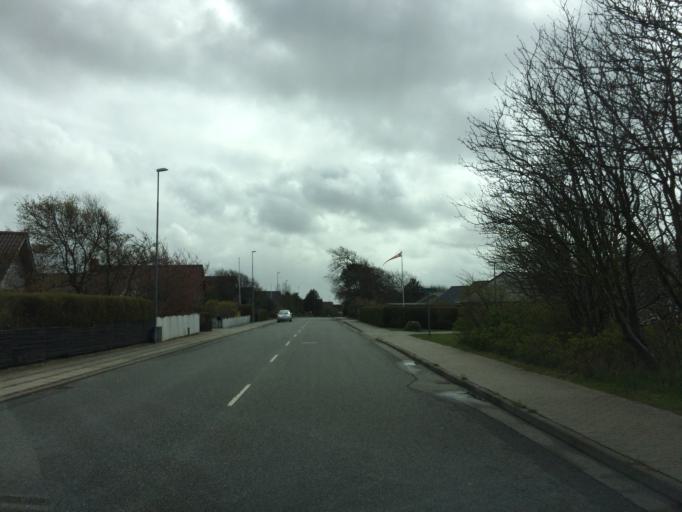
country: DK
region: South Denmark
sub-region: Fano Kommune
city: Nordby
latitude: 55.5324
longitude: 8.3481
